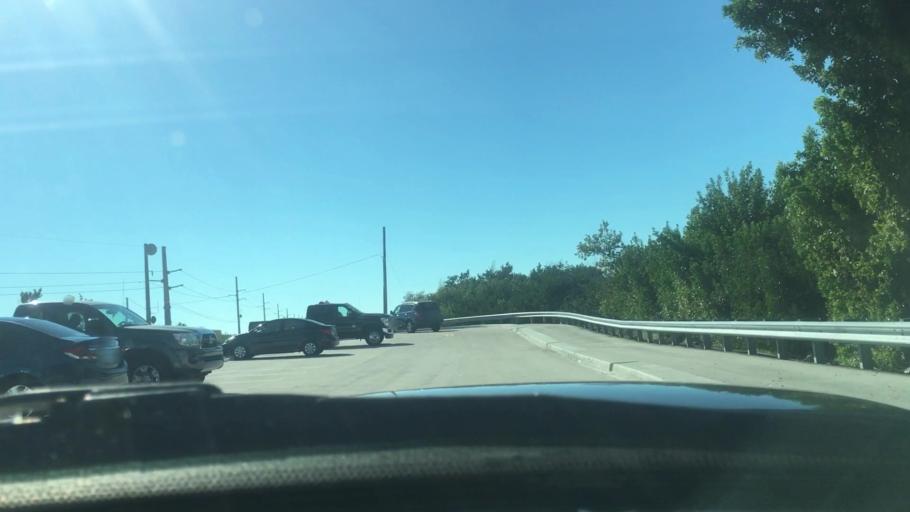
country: US
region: Florida
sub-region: Monroe County
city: Big Pine Key
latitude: 24.6820
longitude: -81.2304
